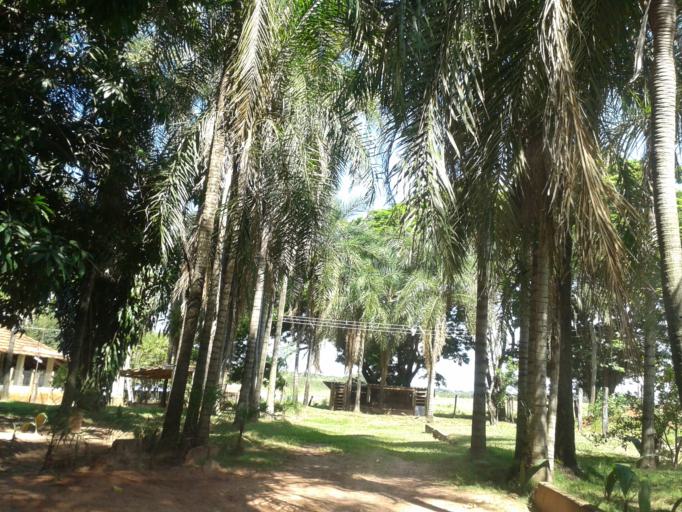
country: BR
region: Minas Gerais
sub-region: Santa Vitoria
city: Santa Vitoria
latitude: -19.1233
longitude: -50.5015
